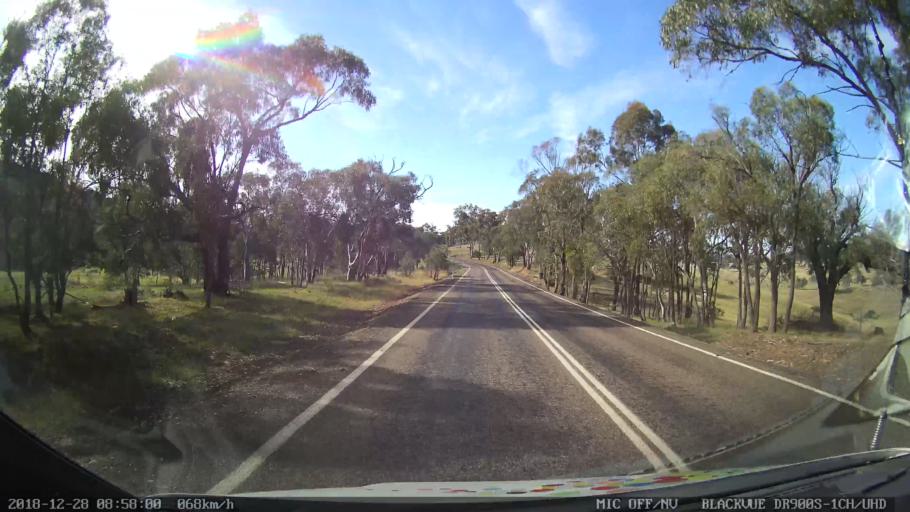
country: AU
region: New South Wales
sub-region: Upper Lachlan Shire
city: Crookwell
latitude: -34.1233
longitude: 149.3320
